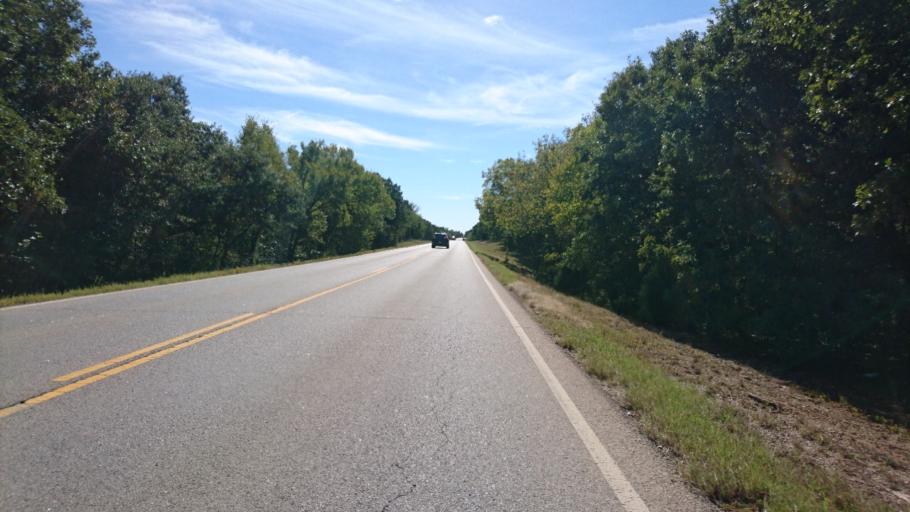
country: US
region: Oklahoma
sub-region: Lincoln County
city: Stroud
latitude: 35.7293
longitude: -96.7267
